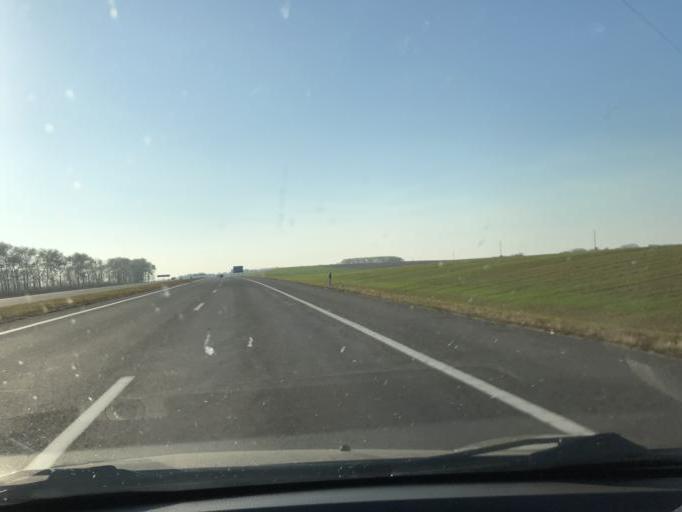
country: BY
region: Minsk
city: Samakhvalavichy
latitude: 53.7319
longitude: 27.5356
